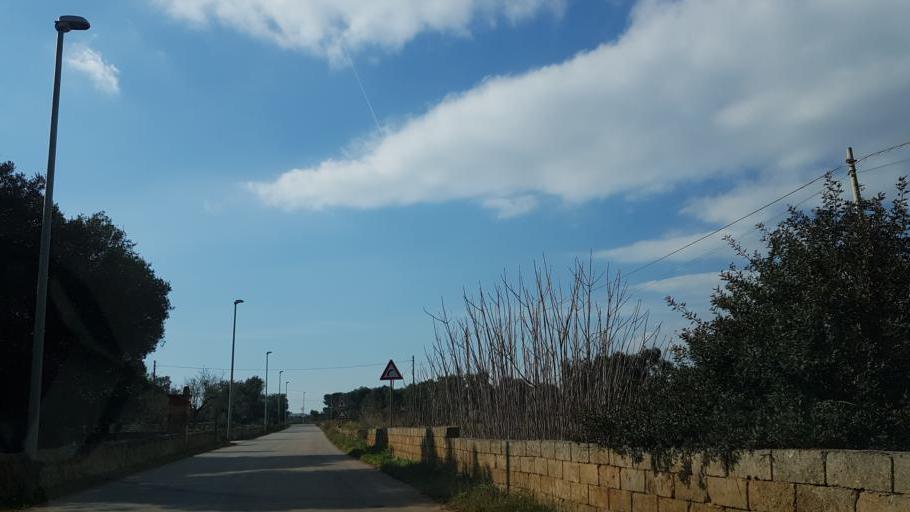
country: IT
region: Apulia
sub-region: Provincia di Brindisi
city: Carovigno
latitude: 40.7114
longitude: 17.6744
